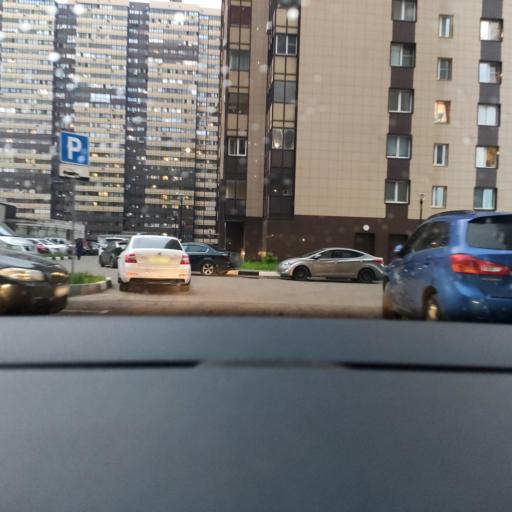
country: RU
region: Moskovskaya
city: Reutov
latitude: 55.7550
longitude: 37.8869
